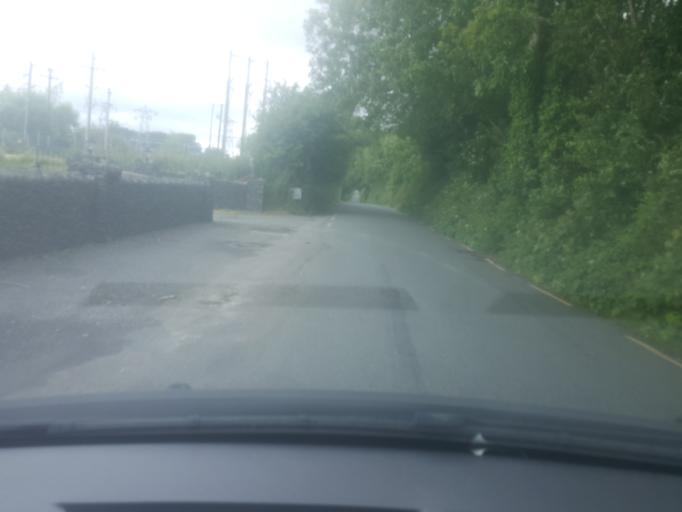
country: IE
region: Munster
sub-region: Ciarrai
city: Cill Airne
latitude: 52.0797
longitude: -9.5071
